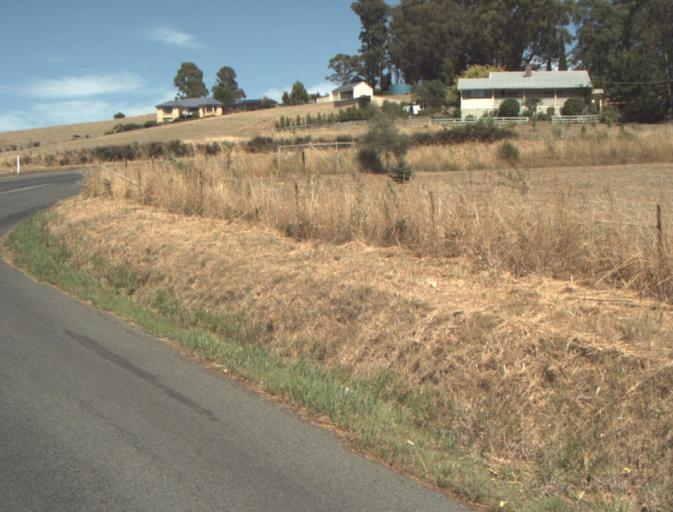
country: AU
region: Tasmania
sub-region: Launceston
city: Mayfield
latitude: -41.2580
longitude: 147.1460
